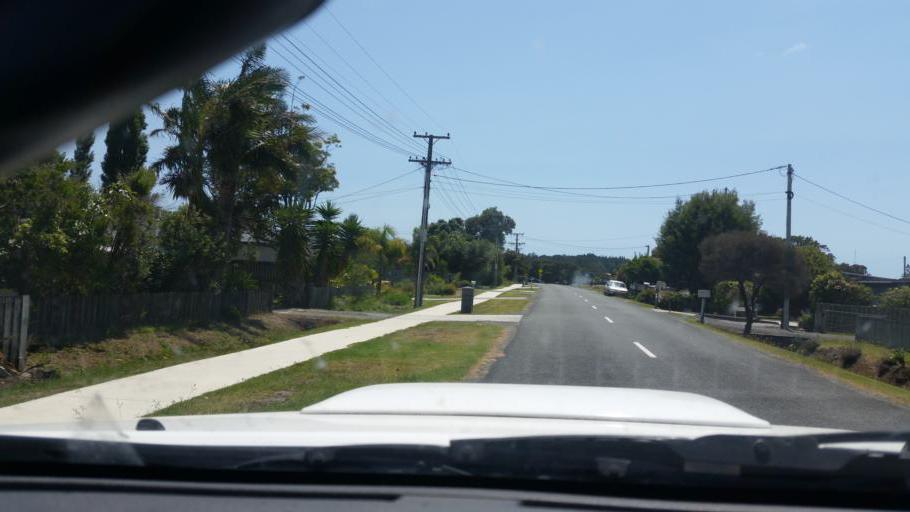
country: NZ
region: Auckland
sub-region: Auckland
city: Wellsford
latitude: -36.1220
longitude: 174.5759
